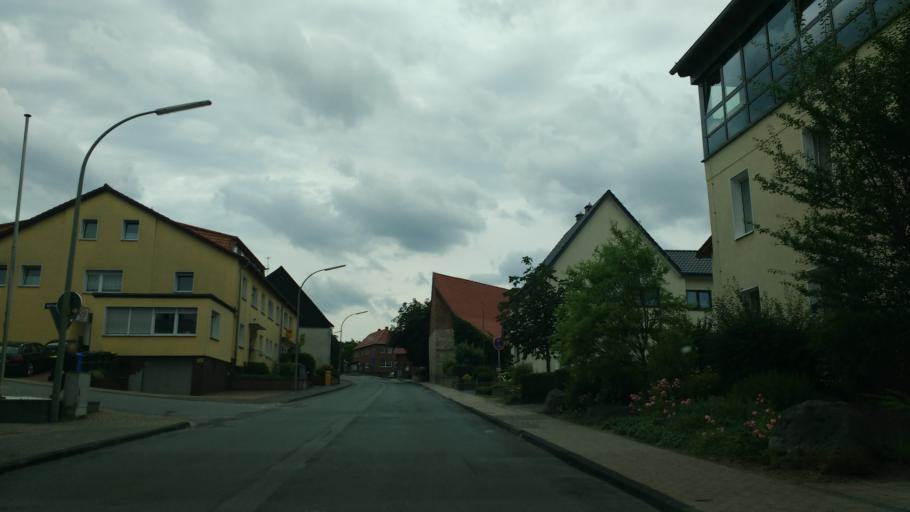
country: DE
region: North Rhine-Westphalia
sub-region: Regierungsbezirk Detmold
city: Wunnenberg
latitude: 51.5658
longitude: 8.7277
